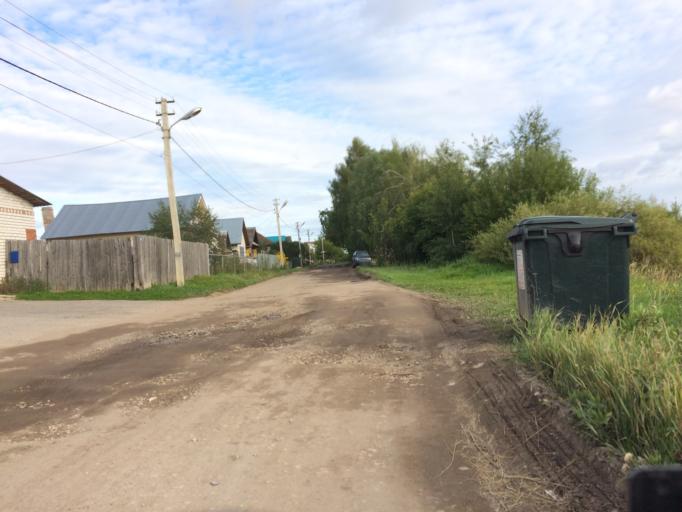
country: RU
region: Mariy-El
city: Yoshkar-Ola
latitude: 56.6548
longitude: 48.0109
